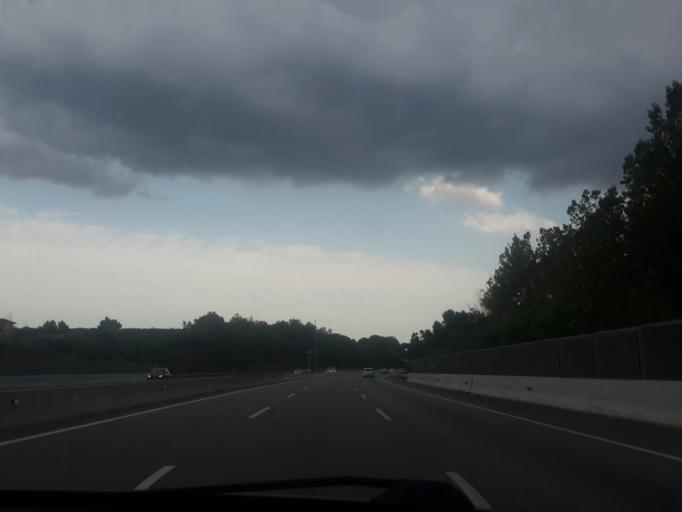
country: ES
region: Catalonia
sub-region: Provincia de Girona
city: Sils
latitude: 41.8353
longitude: 2.7493
